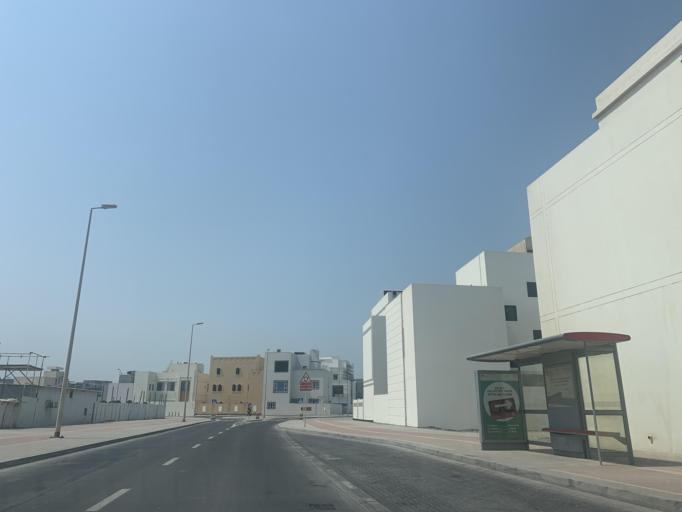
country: BH
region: Muharraq
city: Al Hadd
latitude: 26.2385
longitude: 50.6614
